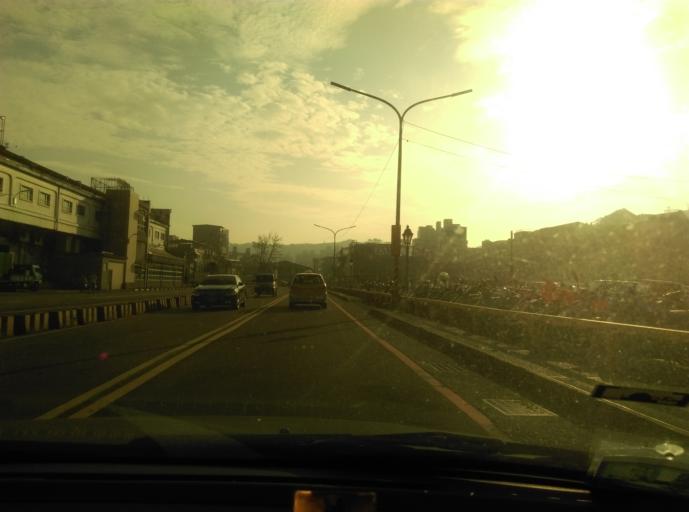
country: TW
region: Taiwan
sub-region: Keelung
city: Keelung
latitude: 25.1354
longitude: 121.7411
